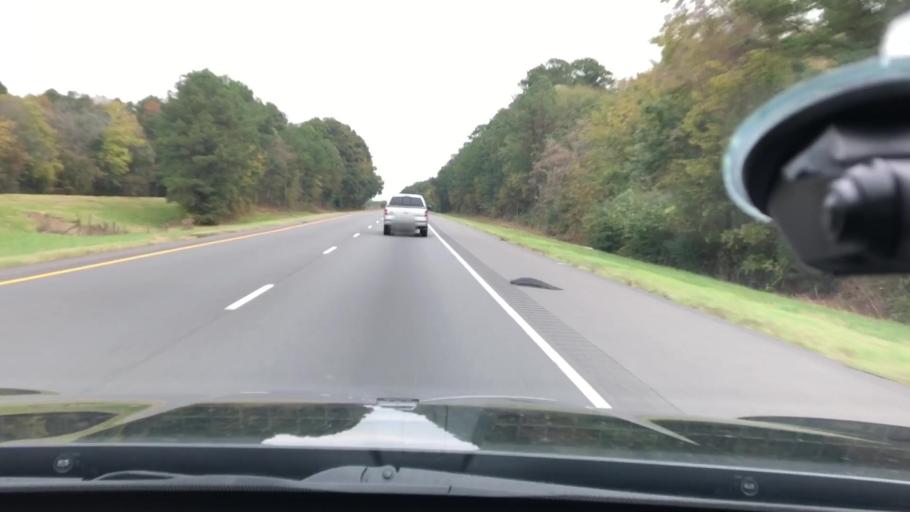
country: US
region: Arkansas
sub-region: Hempstead County
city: Hope
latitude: 33.7301
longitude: -93.5360
